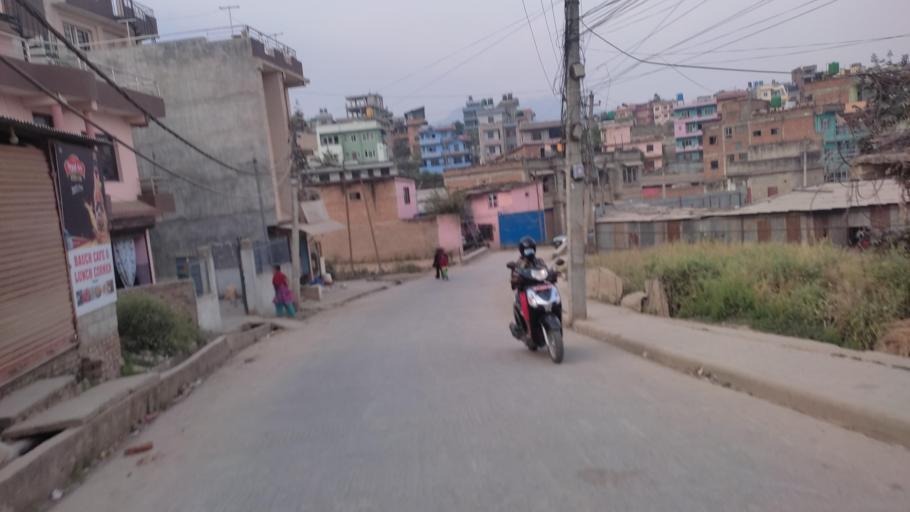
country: NP
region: Central Region
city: Kirtipur
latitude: 27.6817
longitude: 85.2548
